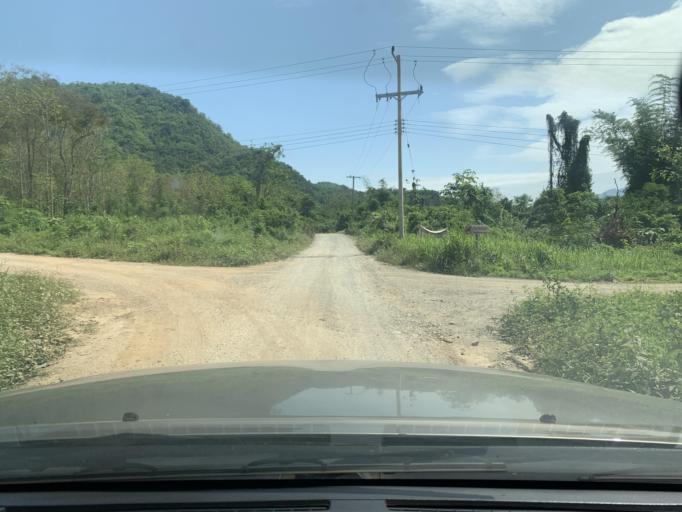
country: LA
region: Louangphabang
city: Louangphabang
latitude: 19.8918
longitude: 102.2016
